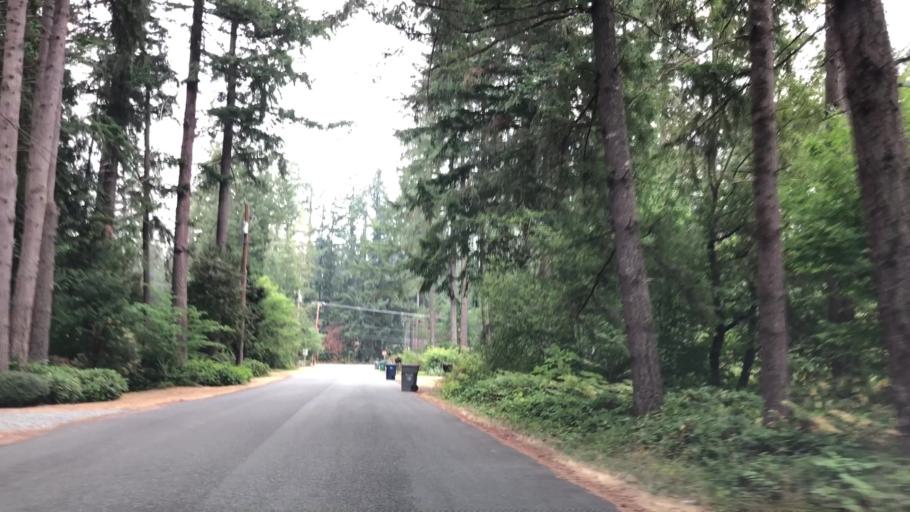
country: US
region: Washington
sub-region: King County
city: Cottage Lake
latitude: 47.7457
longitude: -122.0855
